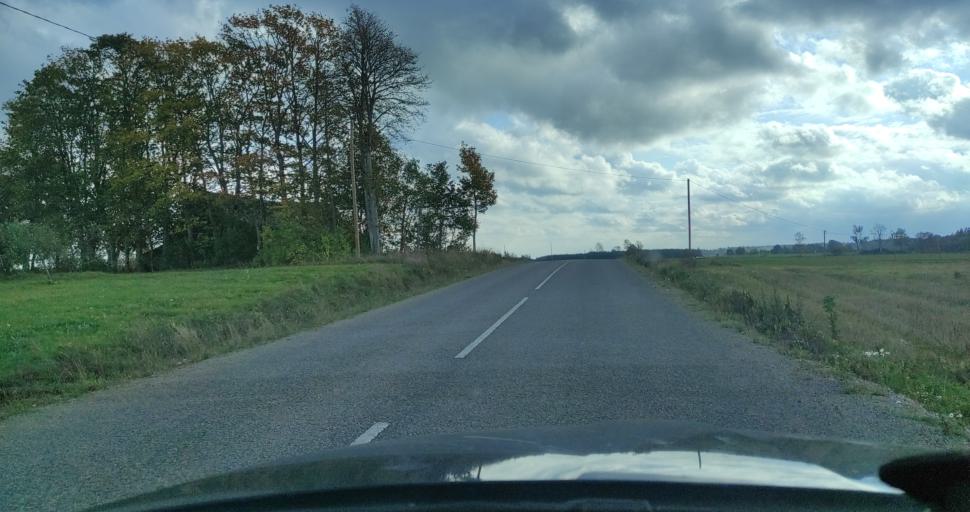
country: LV
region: Talsu Rajons
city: Sabile
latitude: 56.9357
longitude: 22.3968
